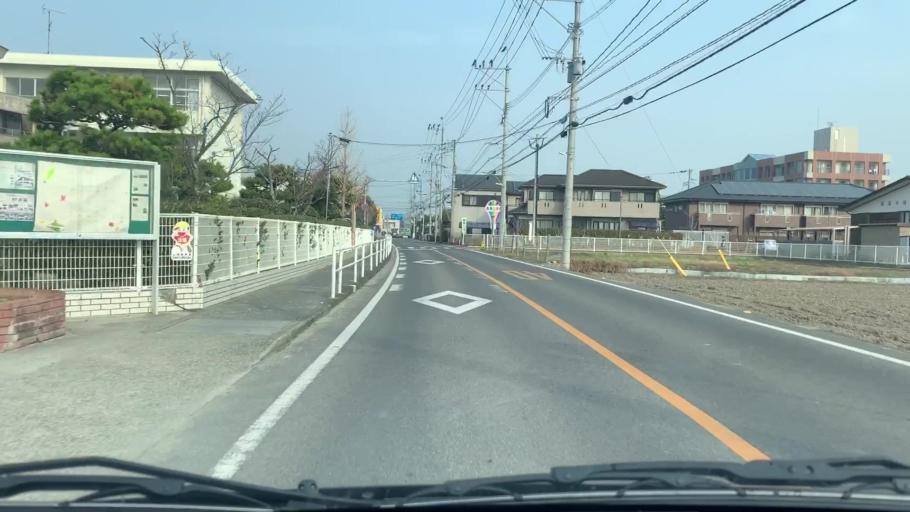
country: JP
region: Saga Prefecture
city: Saga-shi
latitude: 33.2406
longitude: 130.2584
